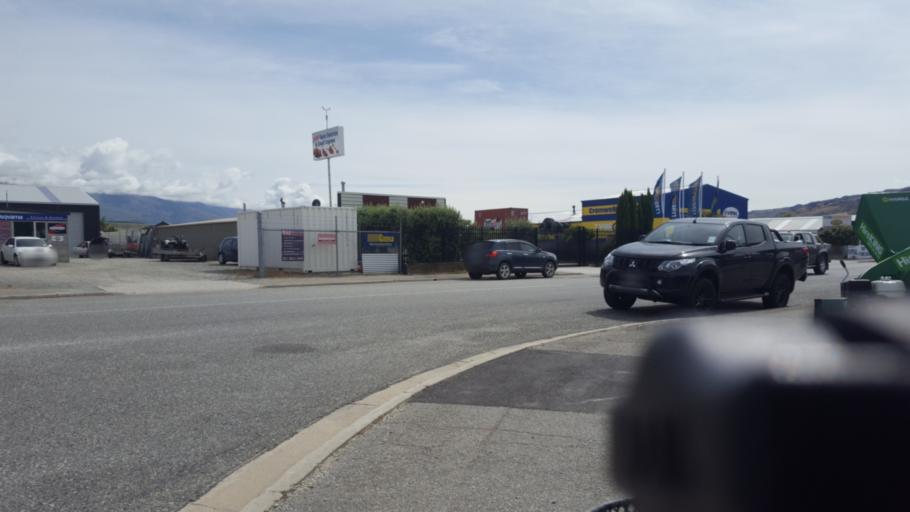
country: NZ
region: Otago
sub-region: Queenstown-Lakes District
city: Wanaka
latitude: -45.0498
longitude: 169.1933
